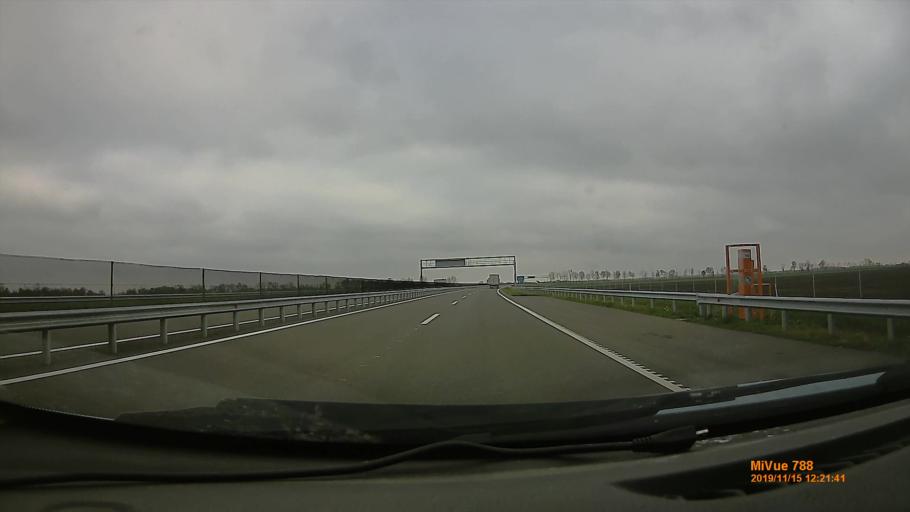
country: HU
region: Bekes
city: Kondoros
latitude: 46.8089
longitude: 20.6859
